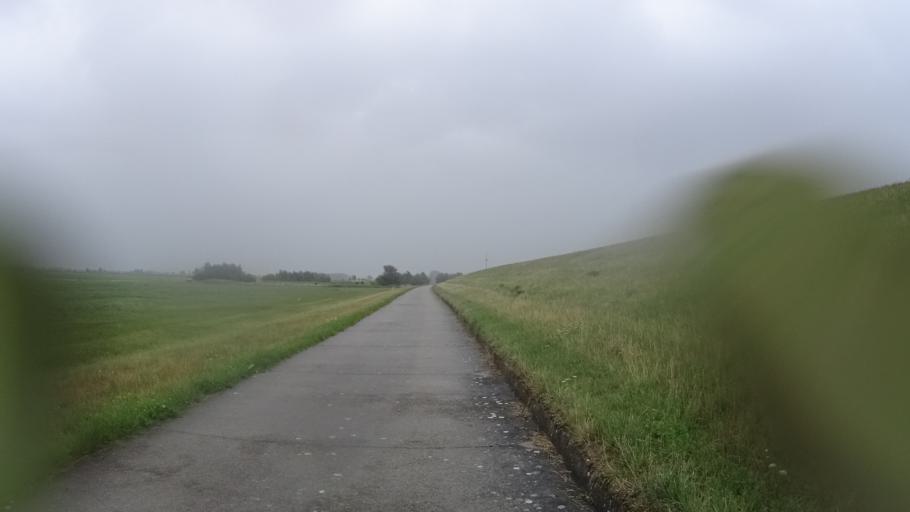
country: DE
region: Lower Saxony
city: Hitzacker
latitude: 53.1803
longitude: 11.0206
